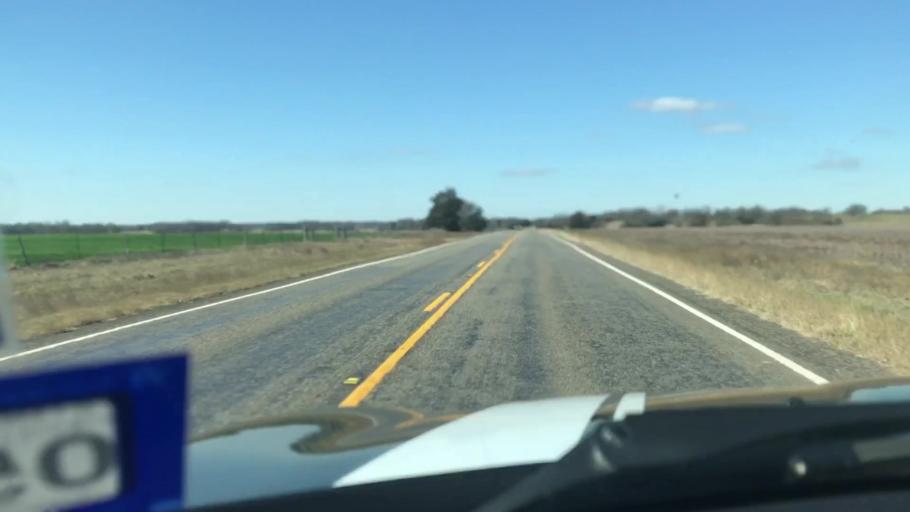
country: US
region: Texas
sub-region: Robertson County
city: Calvert
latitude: 30.8742
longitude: -96.7227
